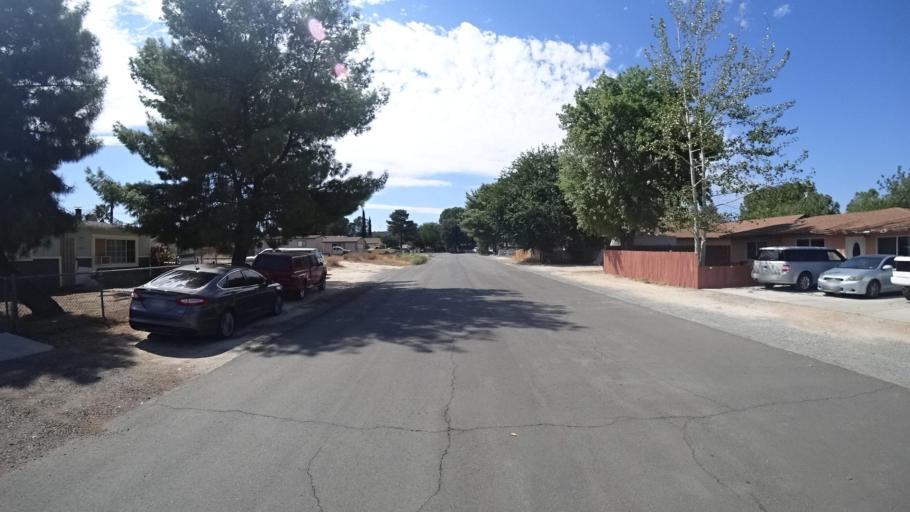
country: MX
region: Baja California
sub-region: Tecate
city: Cereso del Hongo
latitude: 32.6191
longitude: -116.1881
